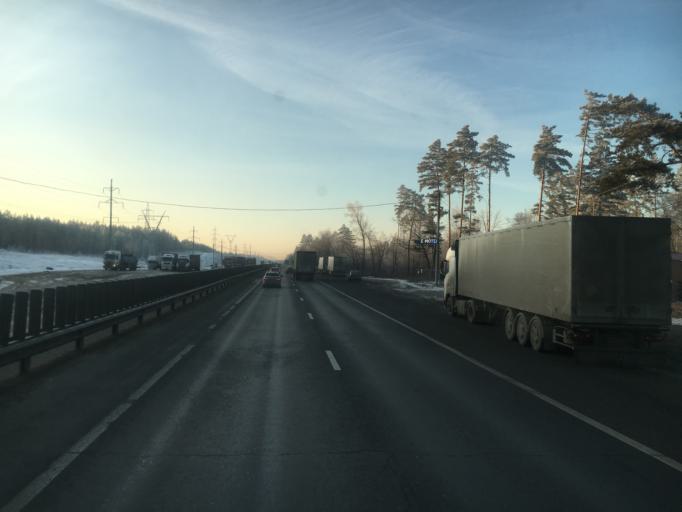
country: RU
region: Samara
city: Pribrezhnyy
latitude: 53.5138
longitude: 49.9033
